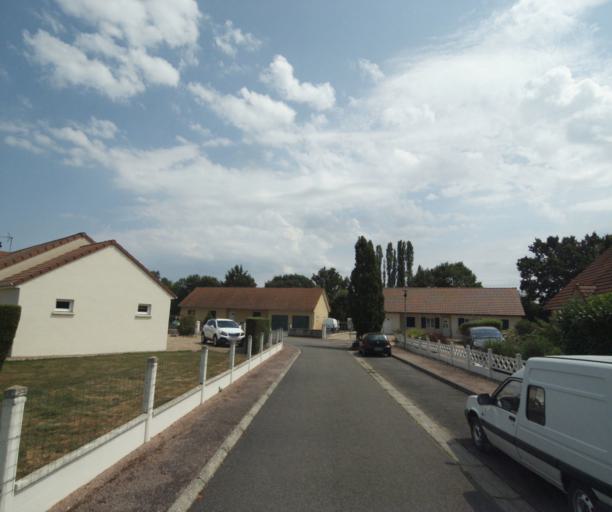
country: FR
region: Bourgogne
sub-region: Departement de Saone-et-Loire
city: Gueugnon
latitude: 46.6007
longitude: 4.0470
